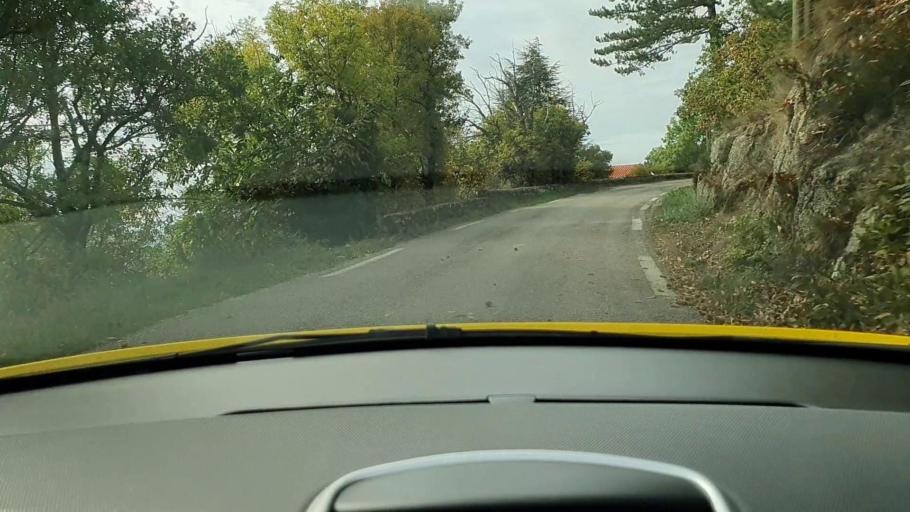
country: FR
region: Languedoc-Roussillon
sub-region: Departement du Gard
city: Le Vigan
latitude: 44.0215
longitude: 3.5746
